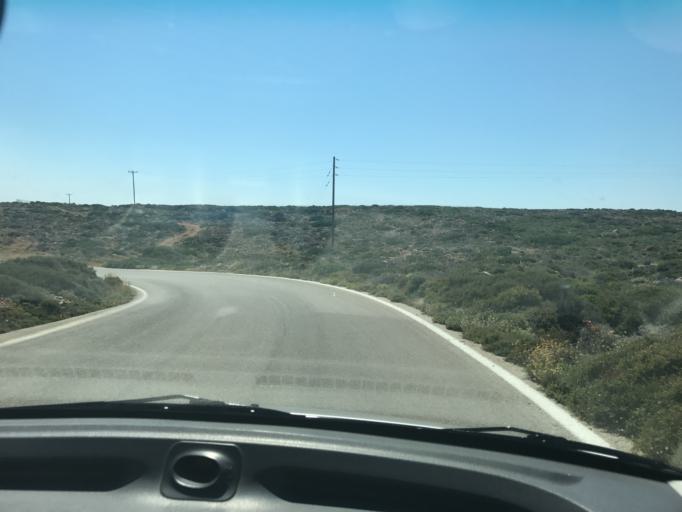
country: GR
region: South Aegean
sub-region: Nomos Dodekanisou
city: Karpathos
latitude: 35.4815
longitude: 27.1537
